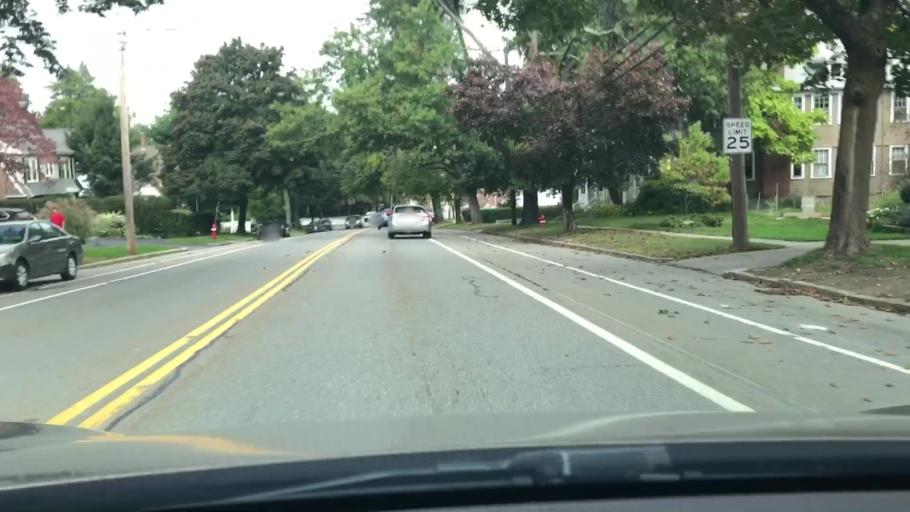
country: US
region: Massachusetts
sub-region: Middlesex County
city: Belmont
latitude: 42.4221
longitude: -71.1832
